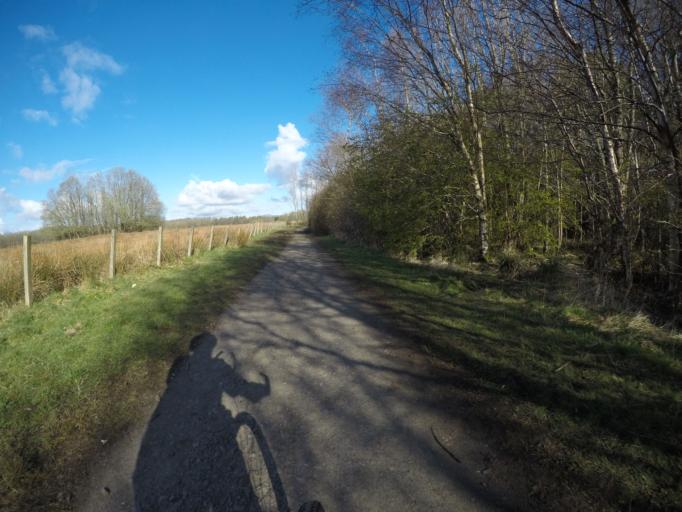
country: GB
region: Scotland
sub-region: North Ayrshire
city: Irvine
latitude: 55.6405
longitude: -4.6577
